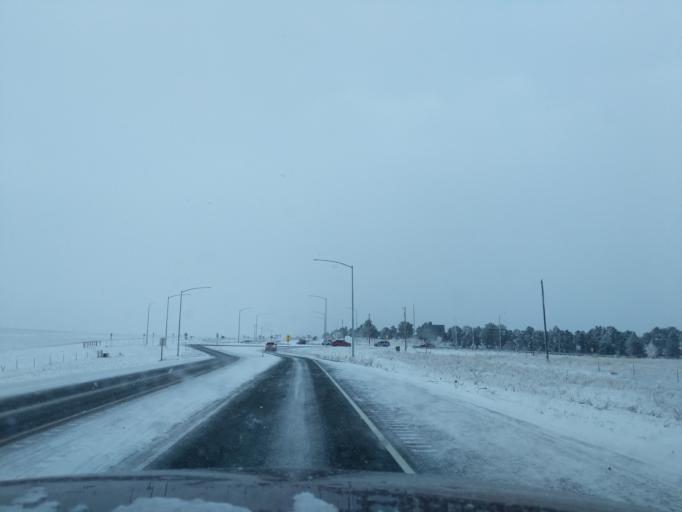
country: US
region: Montana
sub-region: Yellowstone County
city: Billings
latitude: 45.8064
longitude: -108.6018
